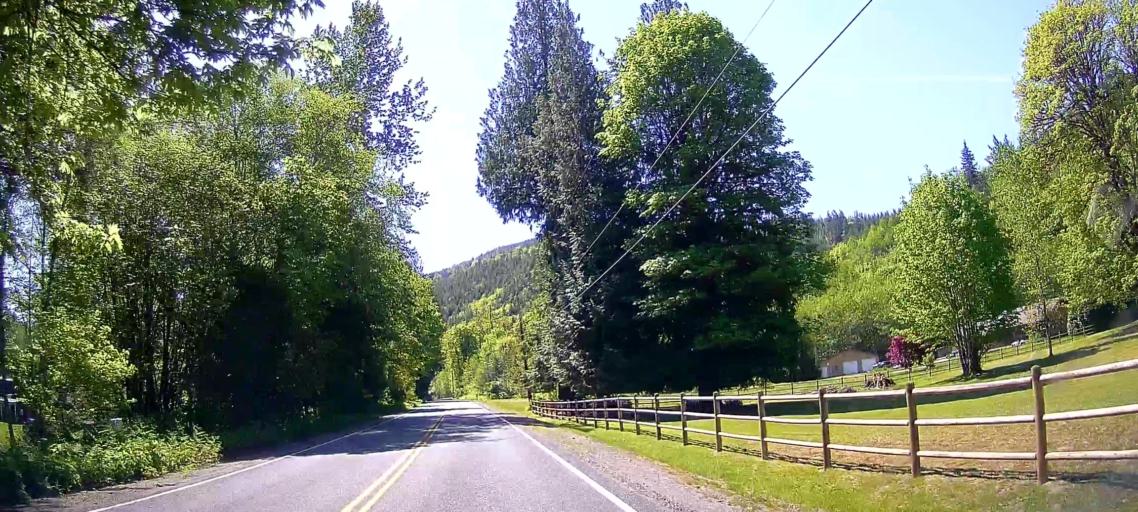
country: US
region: Washington
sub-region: Snohomish County
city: Darrington
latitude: 48.4861
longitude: -121.6550
